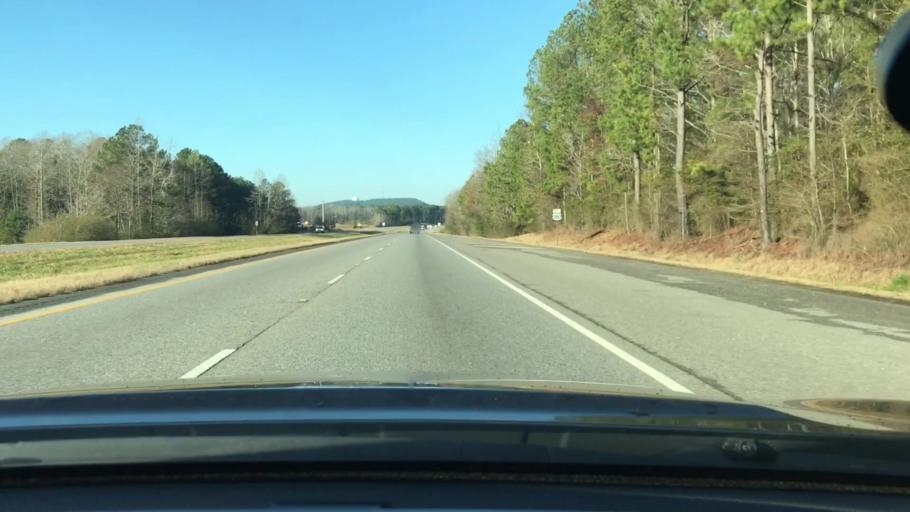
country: US
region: Alabama
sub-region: Shelby County
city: Westover
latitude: 33.3489
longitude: -86.5611
